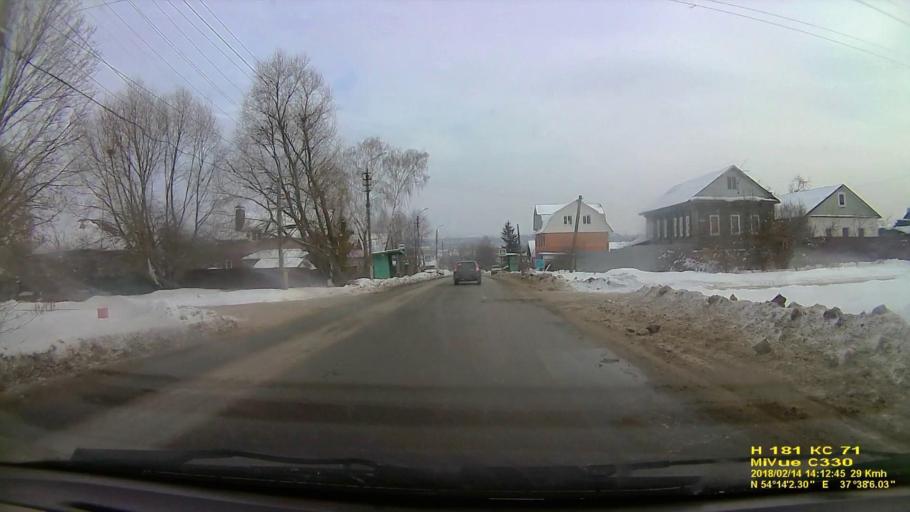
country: RU
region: Tula
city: Gorelki
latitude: 54.2340
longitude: 37.6345
